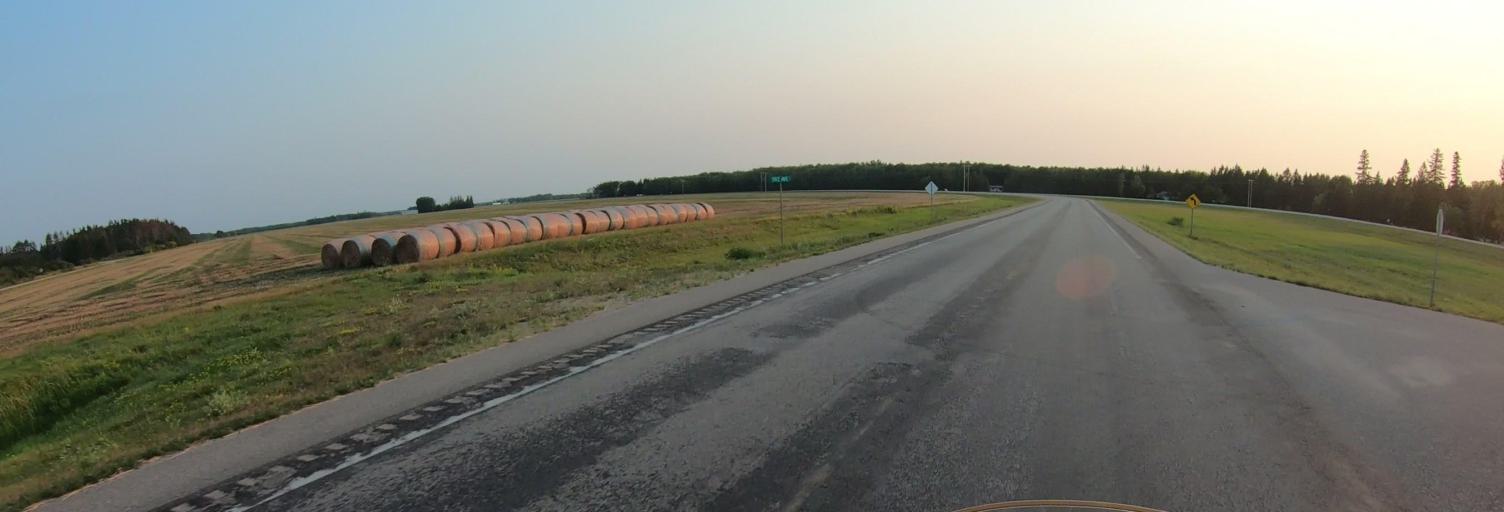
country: US
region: Minnesota
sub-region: Roseau County
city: Warroad
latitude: 48.8695
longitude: -95.3255
